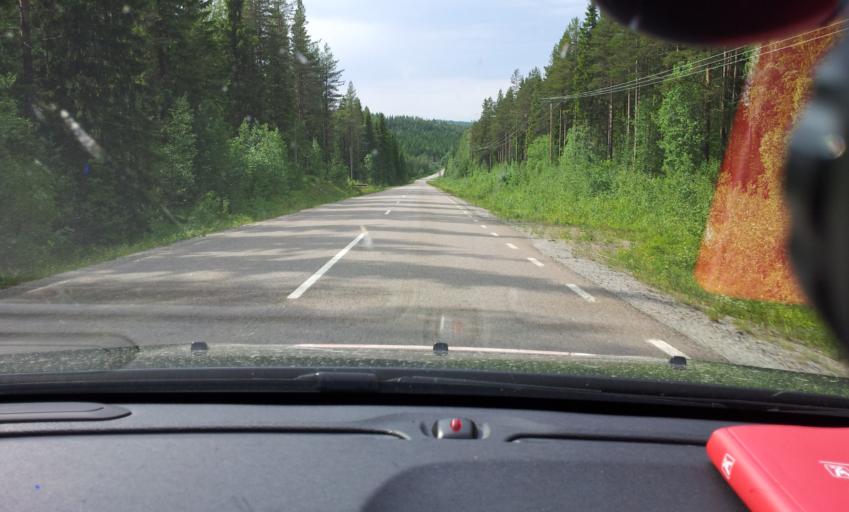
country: SE
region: Jaemtland
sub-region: OEstersunds Kommun
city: Brunflo
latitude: 62.6537
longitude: 14.8906
